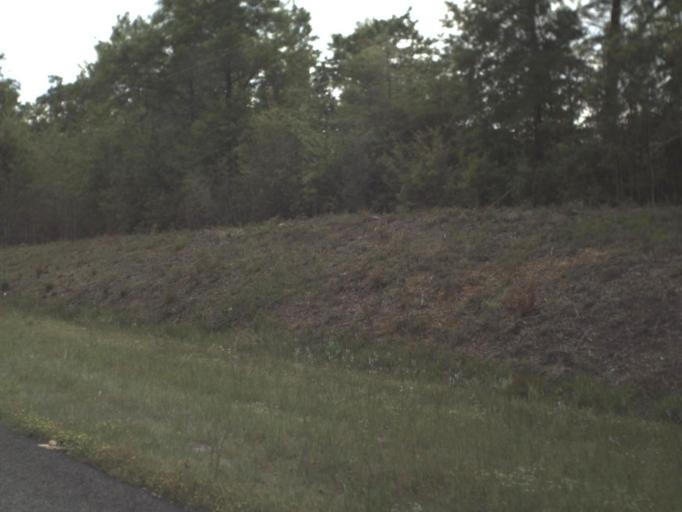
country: US
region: Florida
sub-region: Escambia County
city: Molino
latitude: 30.7817
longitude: -87.3365
